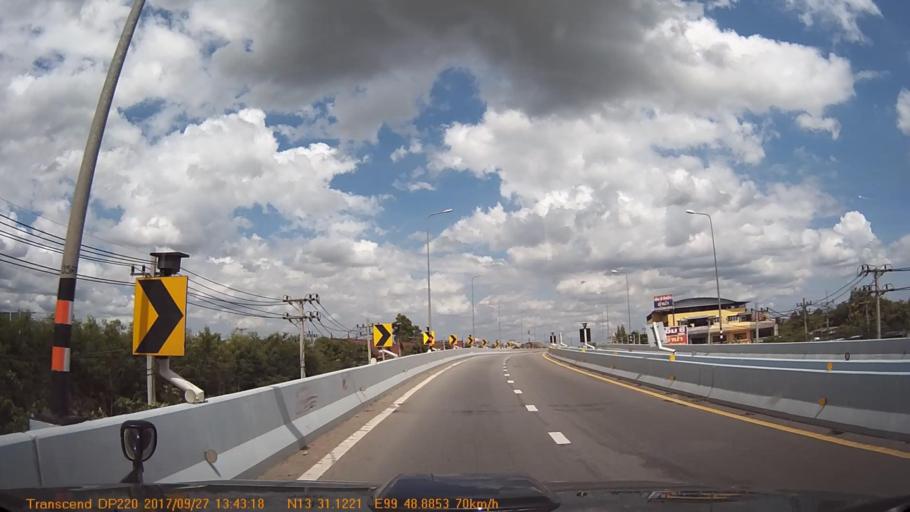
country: TH
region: Ratchaburi
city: Ratchaburi
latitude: 13.5187
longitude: 99.8146
